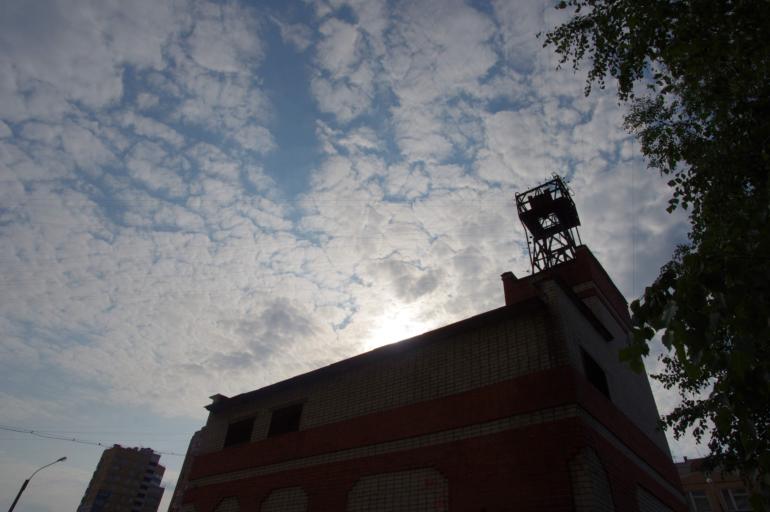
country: RU
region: Nizjnij Novgorod
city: Nizhniy Novgorod
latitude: 56.3422
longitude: 43.9281
